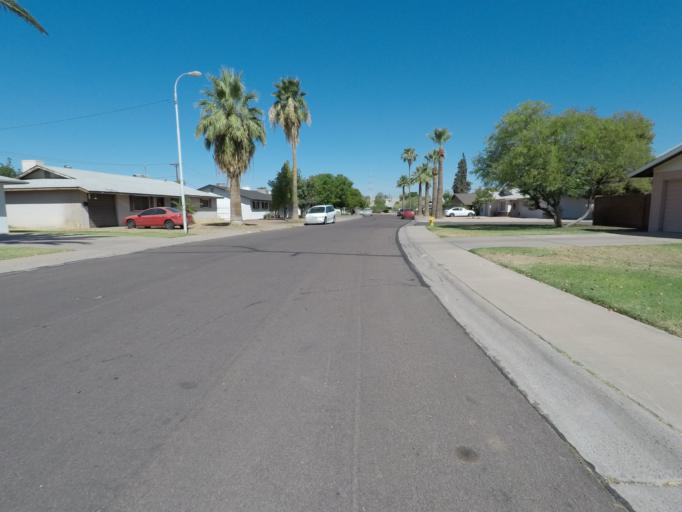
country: US
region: Arizona
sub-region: Maricopa County
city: Tempe Junction
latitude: 33.3980
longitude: -111.9407
